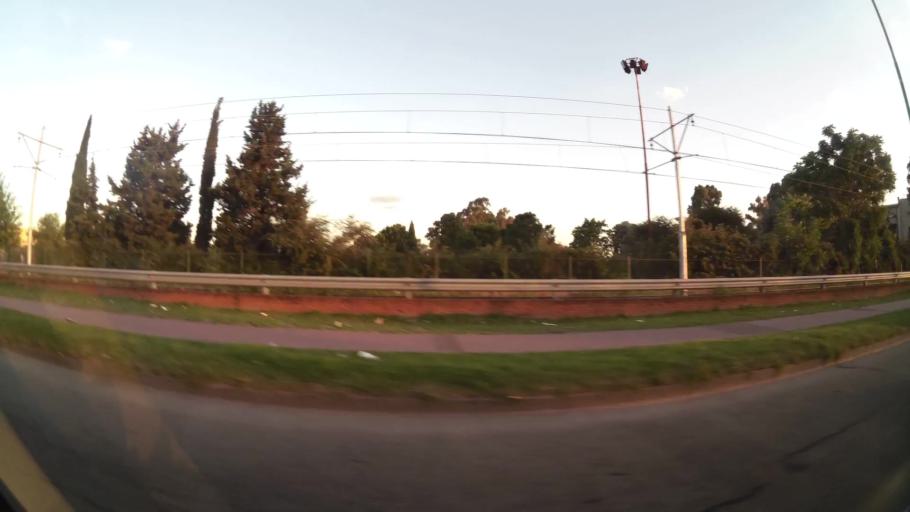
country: AR
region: Buenos Aires F.D.
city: Villa Lugano
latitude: -34.6764
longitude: -58.4627
